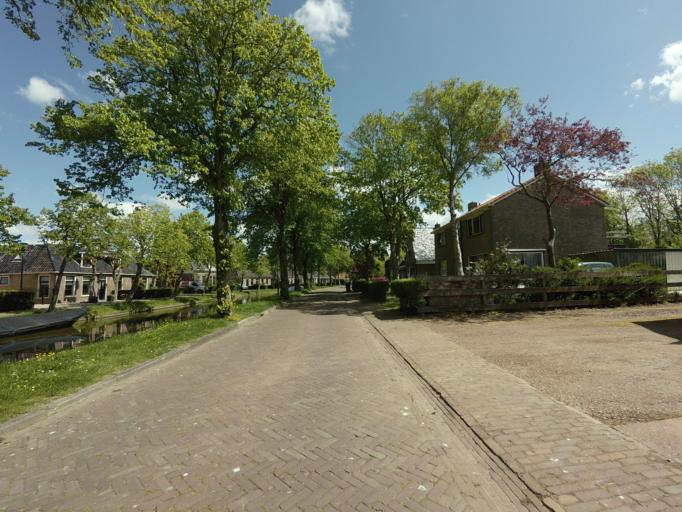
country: NL
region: Friesland
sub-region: Gemeente Harlingen
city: Harlingen
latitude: 53.1497
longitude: 5.4828
